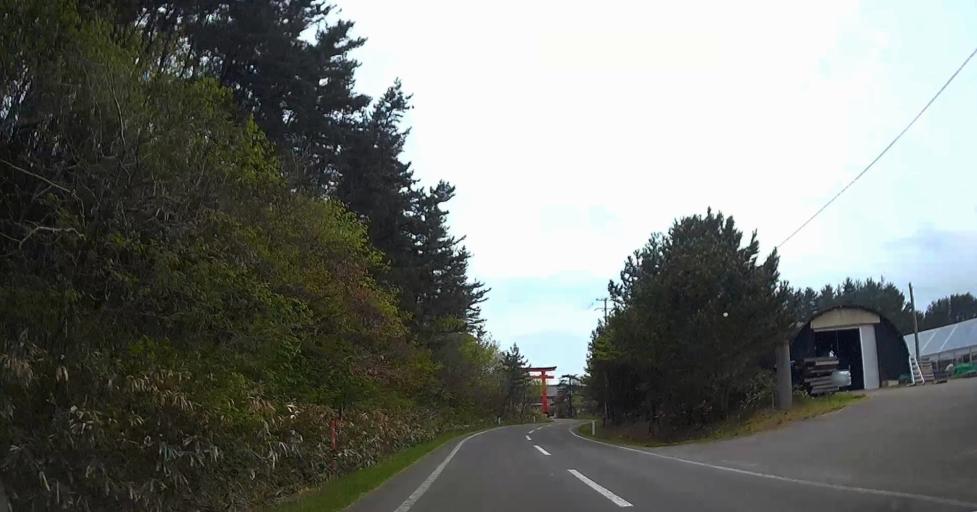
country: JP
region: Aomori
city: Shimokizukuri
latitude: 40.9383
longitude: 140.3151
